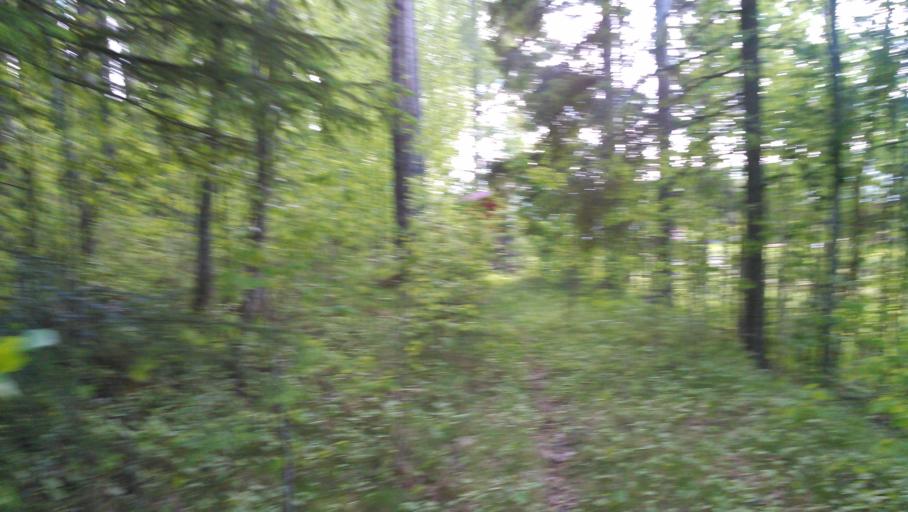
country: SE
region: Vaesterbotten
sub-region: Vannas Kommun
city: Vannasby
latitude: 64.0075
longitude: 19.9181
